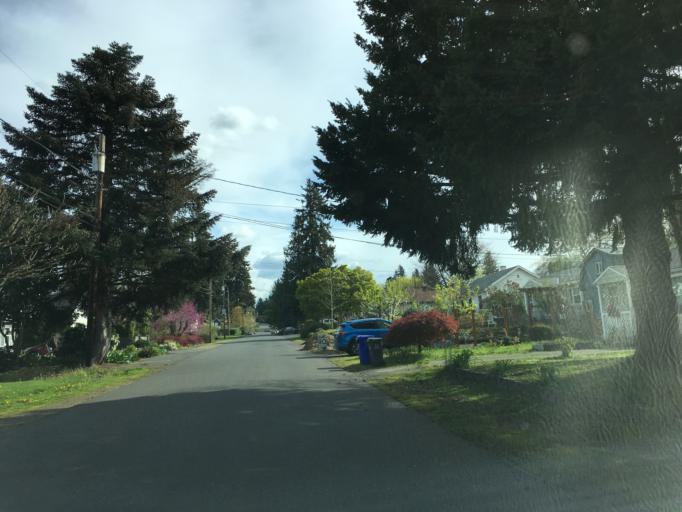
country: US
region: Oregon
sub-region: Multnomah County
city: Lents
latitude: 45.5532
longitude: -122.5507
